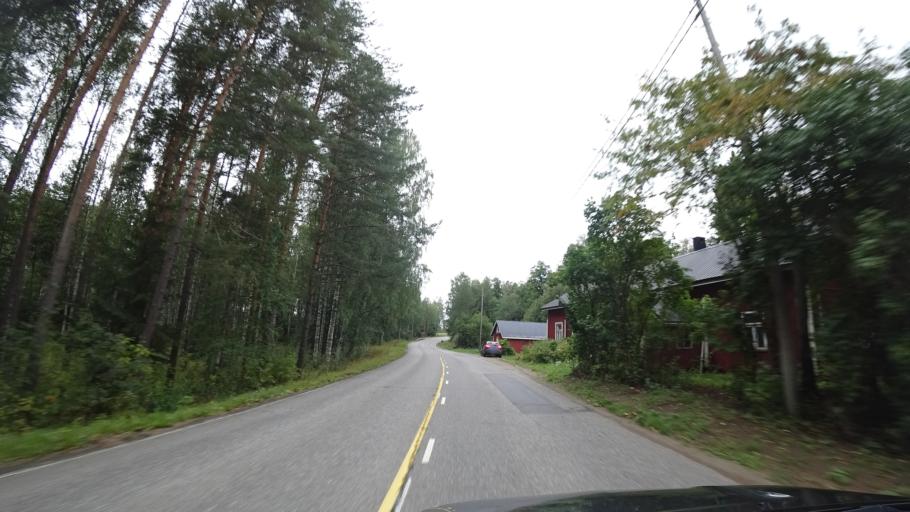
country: FI
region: Haeme
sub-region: Haemeenlinna
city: Lammi
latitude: 61.1206
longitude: 24.9844
